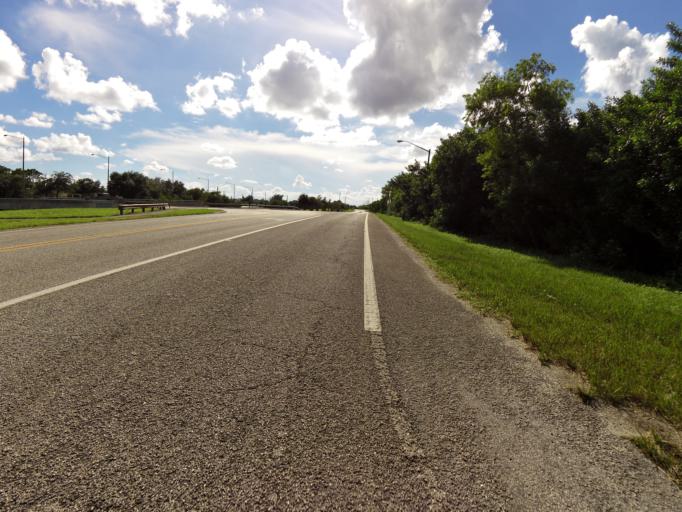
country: US
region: Florida
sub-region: Broward County
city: Sunshine Ranches
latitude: 26.0643
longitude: -80.3100
